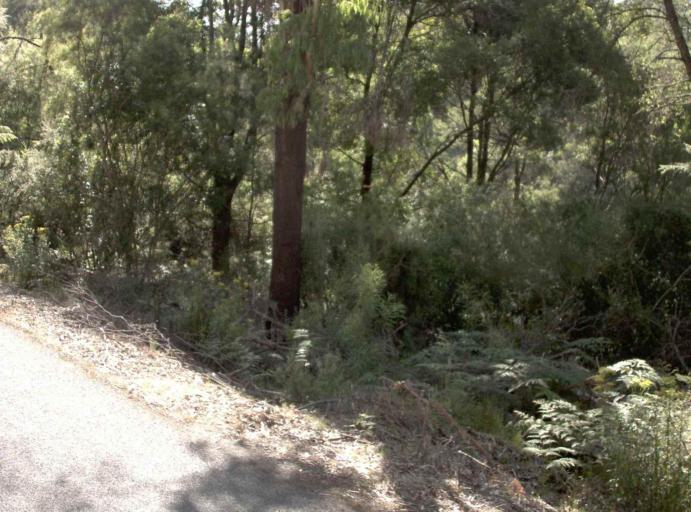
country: AU
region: Victoria
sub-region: East Gippsland
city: Lakes Entrance
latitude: -37.5044
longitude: 148.5355
